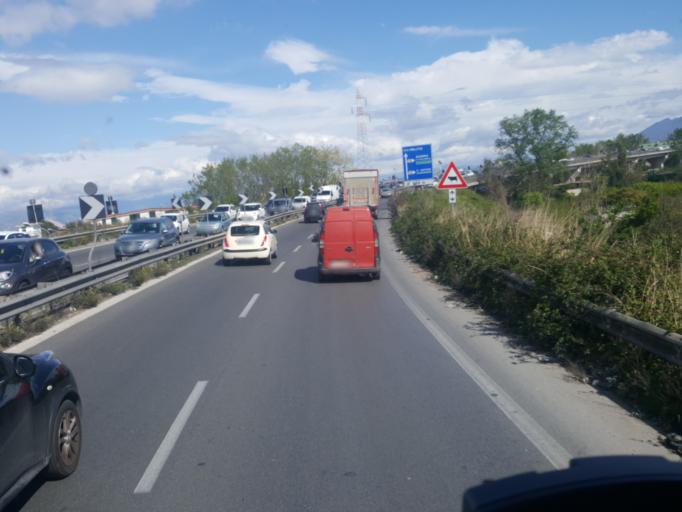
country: IT
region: Campania
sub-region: Provincia di Napoli
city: Sant'Antimo
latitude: 40.9340
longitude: 14.2282
